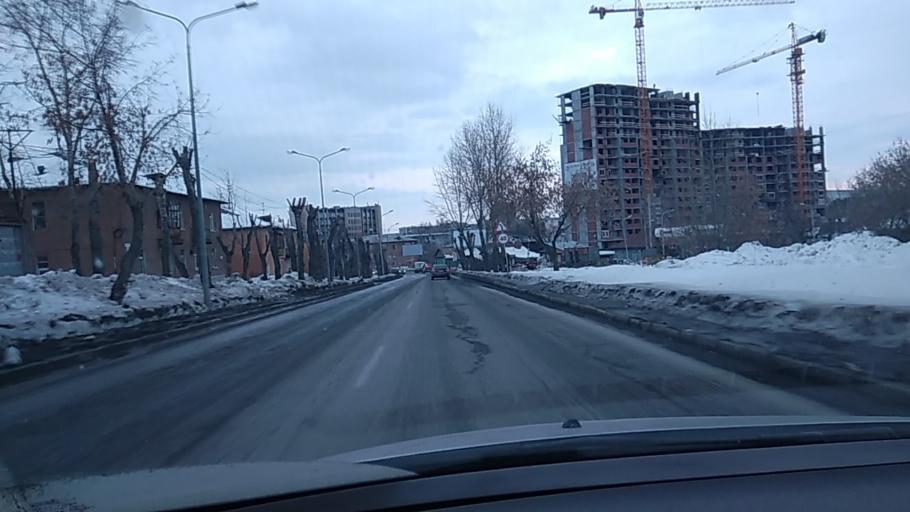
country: RU
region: Sverdlovsk
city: Sovkhoznyy
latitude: 56.8225
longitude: 60.5520
